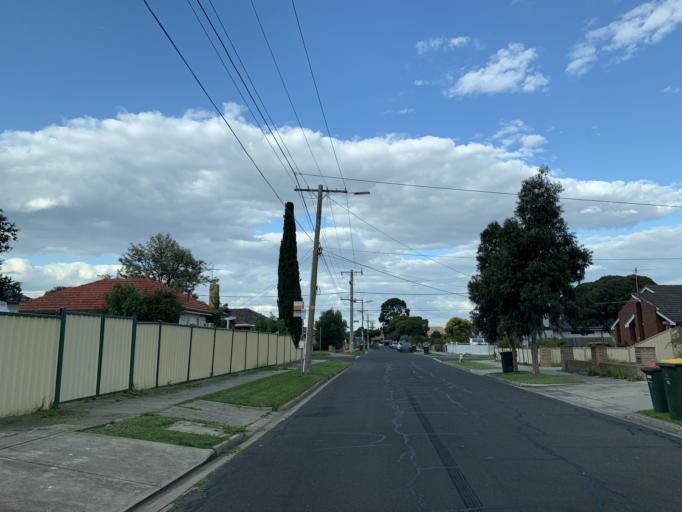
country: AU
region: Victoria
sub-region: Moonee Valley
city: Essendon West
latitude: -37.7612
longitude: 144.8587
